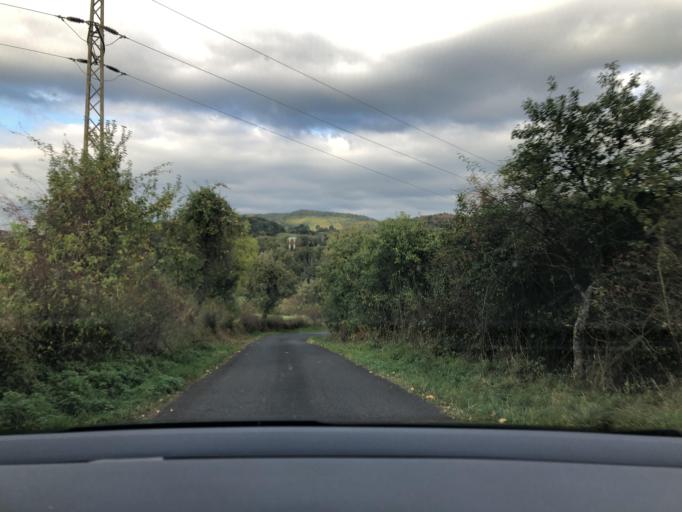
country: CZ
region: Ustecky
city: Velke Brezno
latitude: 50.6276
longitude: 14.1613
